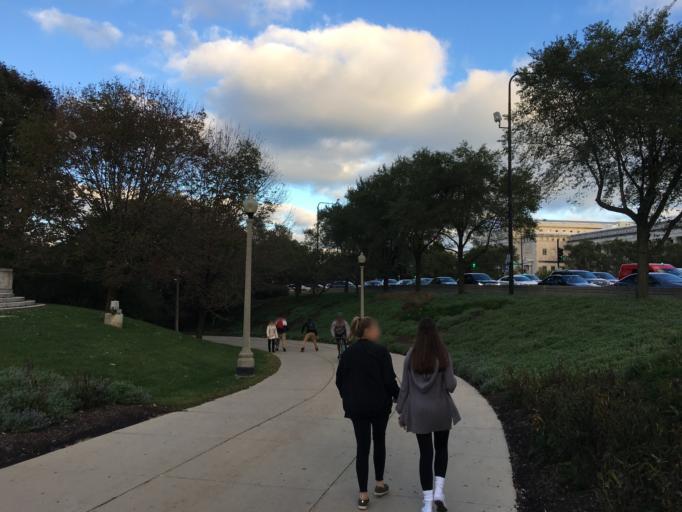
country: US
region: Illinois
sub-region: Cook County
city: Chicago
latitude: 41.8679
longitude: -87.6199
